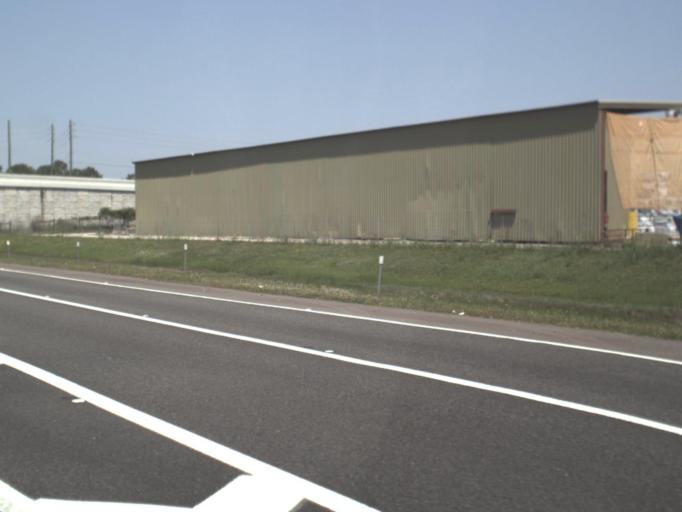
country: US
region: Florida
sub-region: Duval County
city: Baldwin
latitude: 30.3078
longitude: -81.8681
